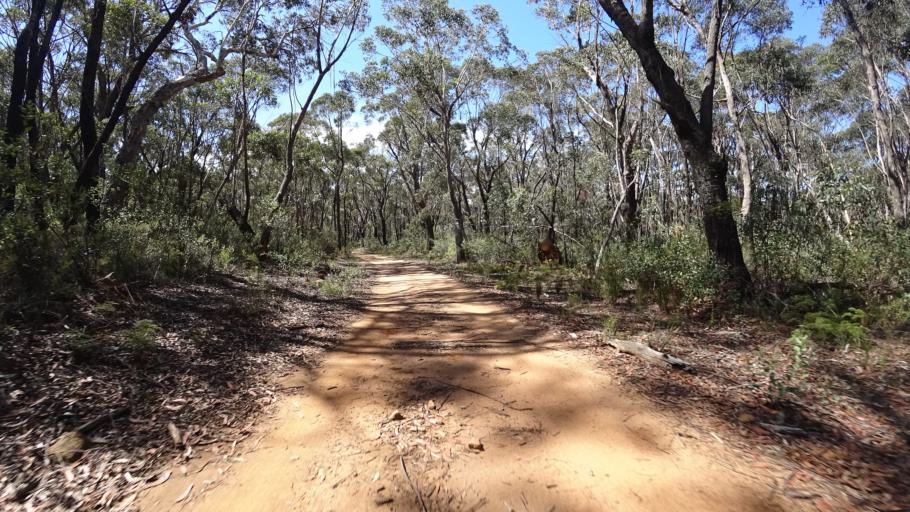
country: AU
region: New South Wales
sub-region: Lithgow
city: Lithgow
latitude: -33.3348
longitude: 150.2869
